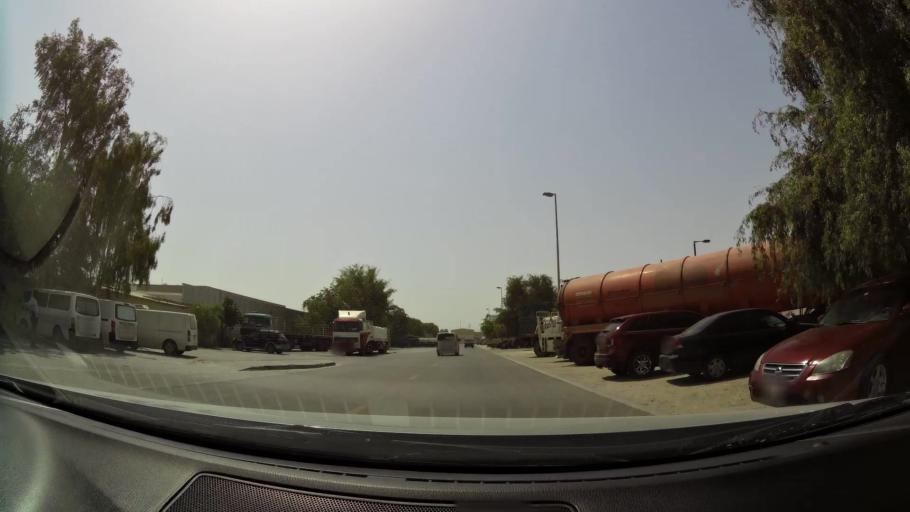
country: AE
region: Dubai
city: Dubai
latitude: 25.1502
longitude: 55.2375
